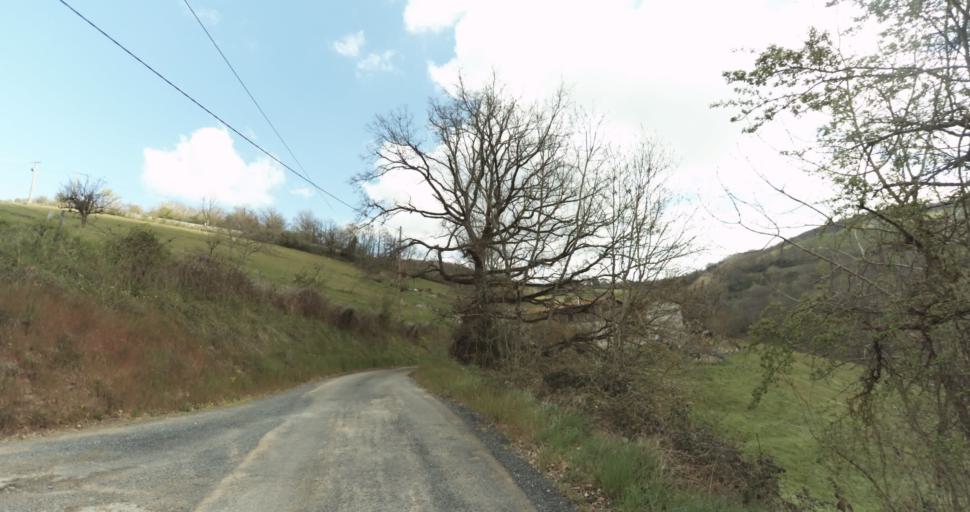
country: FR
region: Rhone-Alpes
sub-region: Departement du Rhone
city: Tarare
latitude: 45.9106
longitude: 4.4300
